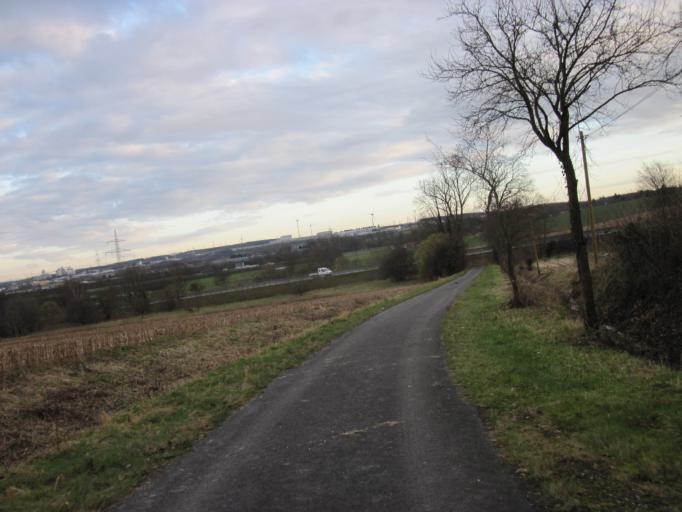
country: DE
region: North Rhine-Westphalia
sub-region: Regierungsbezirk Detmold
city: Paderborn
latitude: 51.7001
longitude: 8.6878
